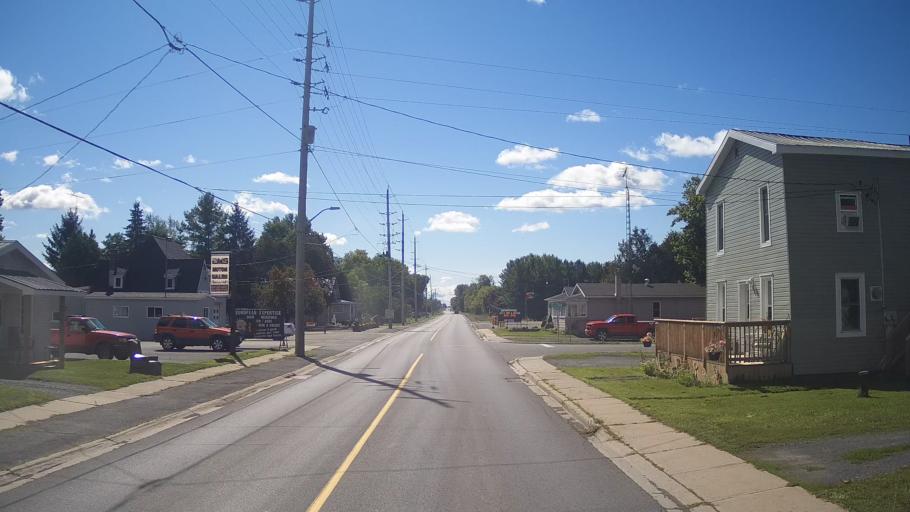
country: US
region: New York
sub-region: St. Lawrence County
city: Norfolk
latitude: 44.9734
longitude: -75.2426
